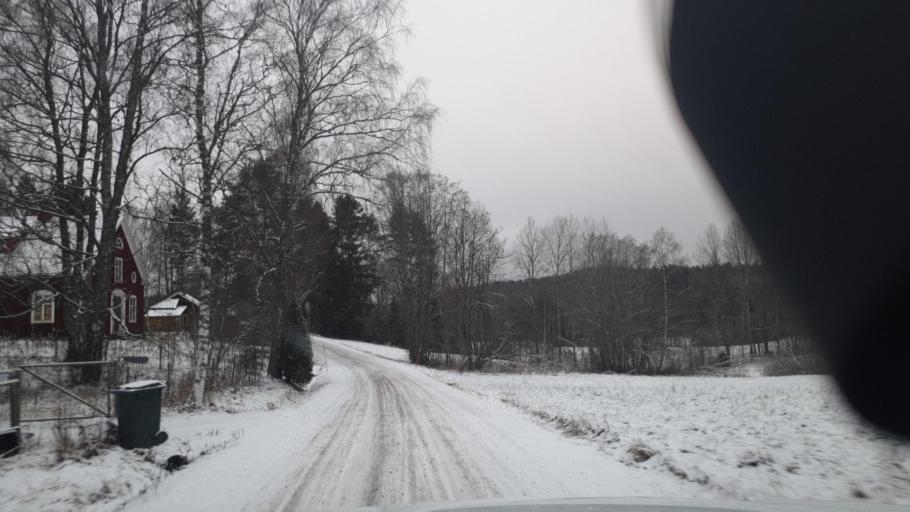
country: SE
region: Vaermland
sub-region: Karlstads Kommun
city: Edsvalla
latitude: 59.6169
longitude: 13.0673
